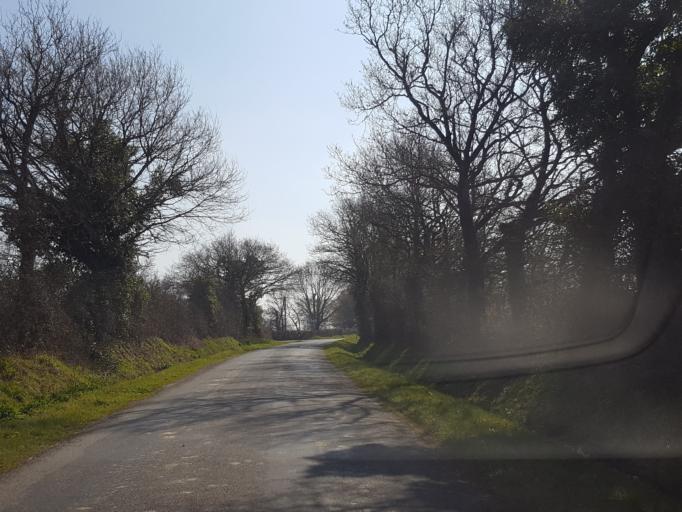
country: FR
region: Pays de la Loire
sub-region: Departement de la Vendee
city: La Chaize-le-Vicomte
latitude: 46.6619
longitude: -1.3130
